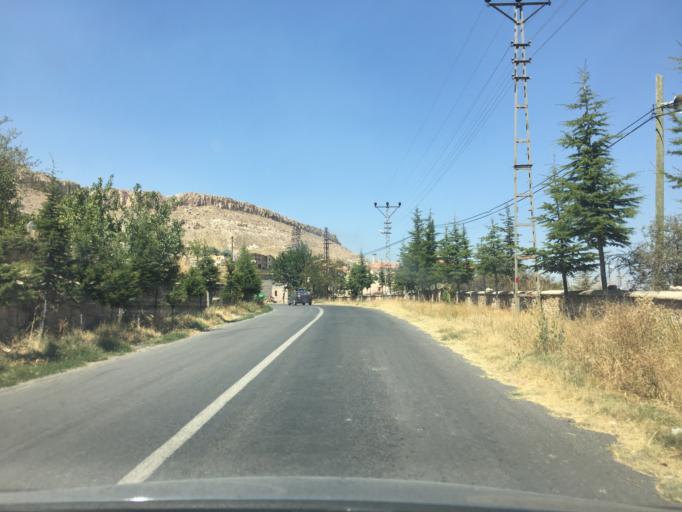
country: TR
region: Nevsehir
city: Urgub
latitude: 38.4695
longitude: 34.9515
